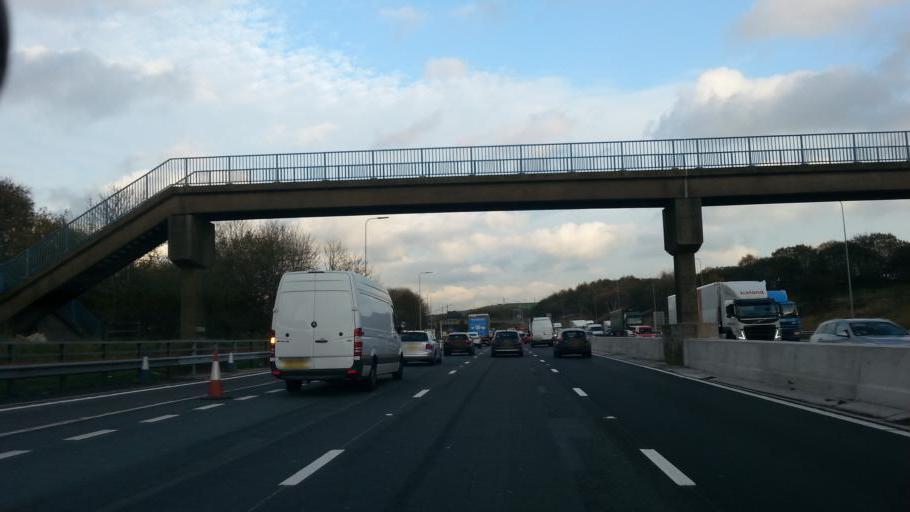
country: GB
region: England
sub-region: Borough of Rochdale
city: Rochdale
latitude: 53.5861
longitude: -2.1685
